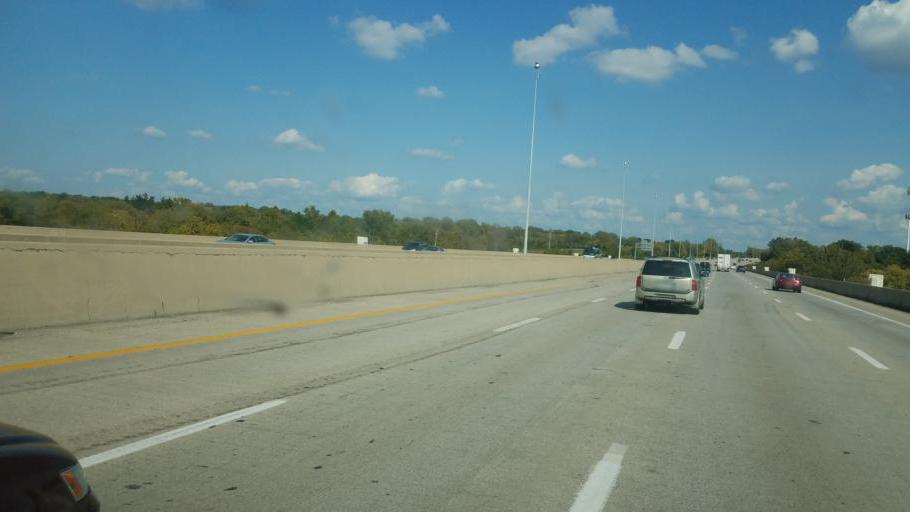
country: US
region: Ohio
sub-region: Franklin County
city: Dublin
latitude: 40.1085
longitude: -83.1146
